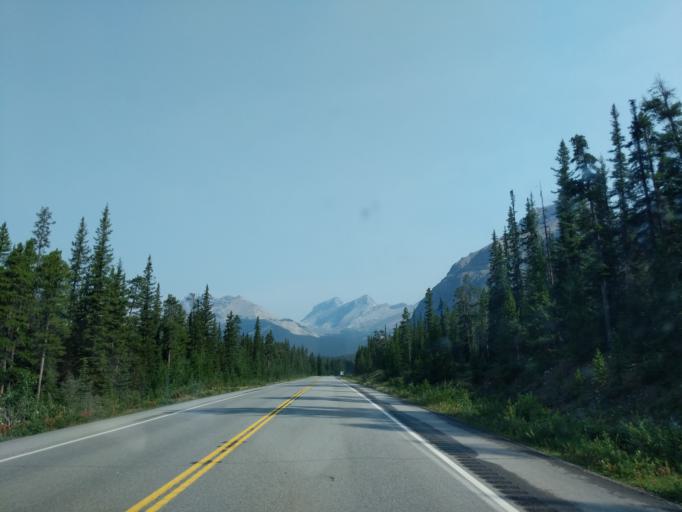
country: CA
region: Alberta
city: Lake Louise
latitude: 51.6109
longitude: -116.3140
